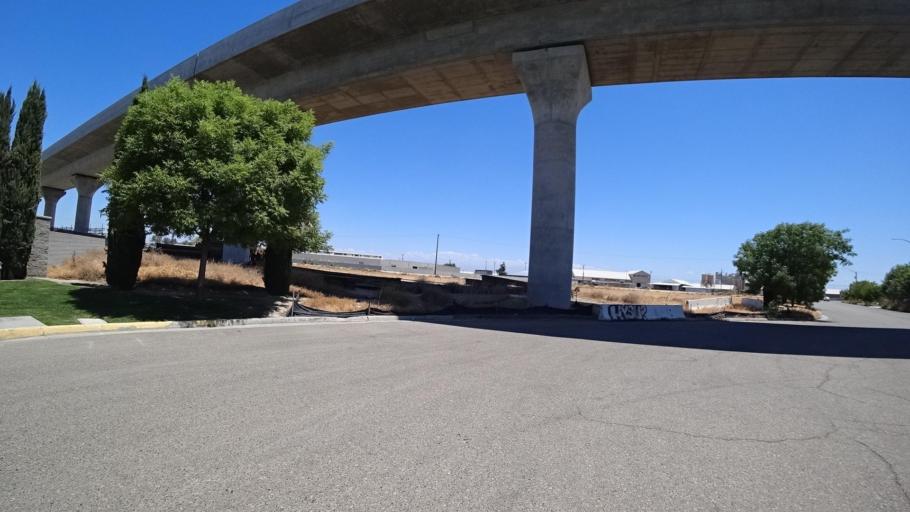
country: US
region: California
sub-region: Fresno County
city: Easton
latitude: 36.6938
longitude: -119.7569
